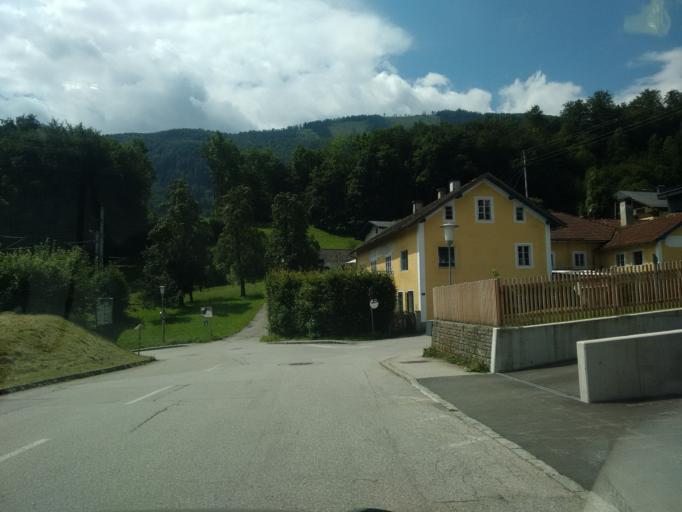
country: AT
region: Upper Austria
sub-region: Politischer Bezirk Gmunden
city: Ebensee
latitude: 47.8541
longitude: 13.7759
